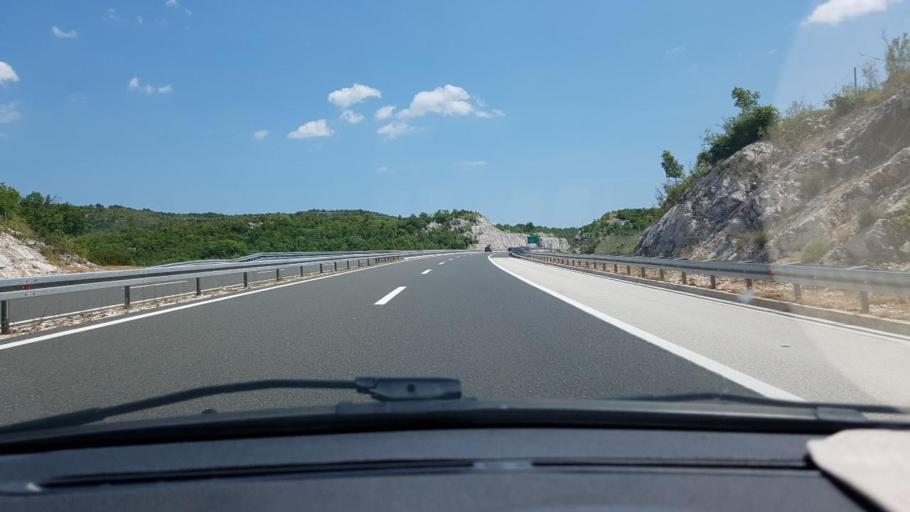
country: HR
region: Splitsko-Dalmatinska
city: Grubine
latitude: 43.3779
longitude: 17.0831
